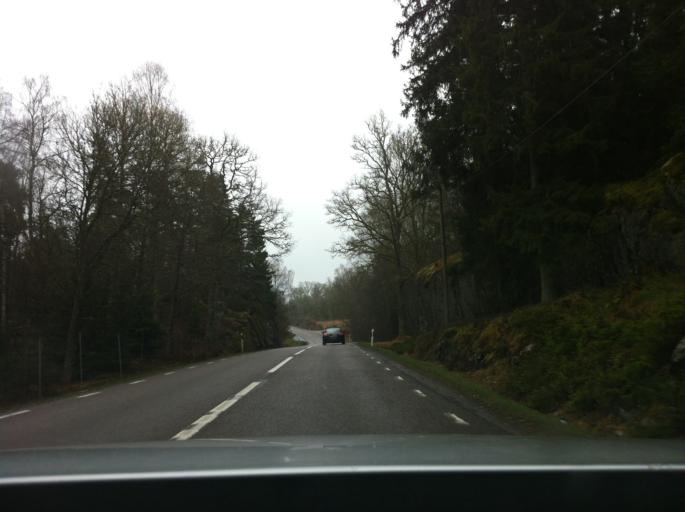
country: SE
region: Vaestra Goetaland
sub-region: Alingsas Kommun
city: Sollebrunn
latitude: 58.1363
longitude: 12.4558
